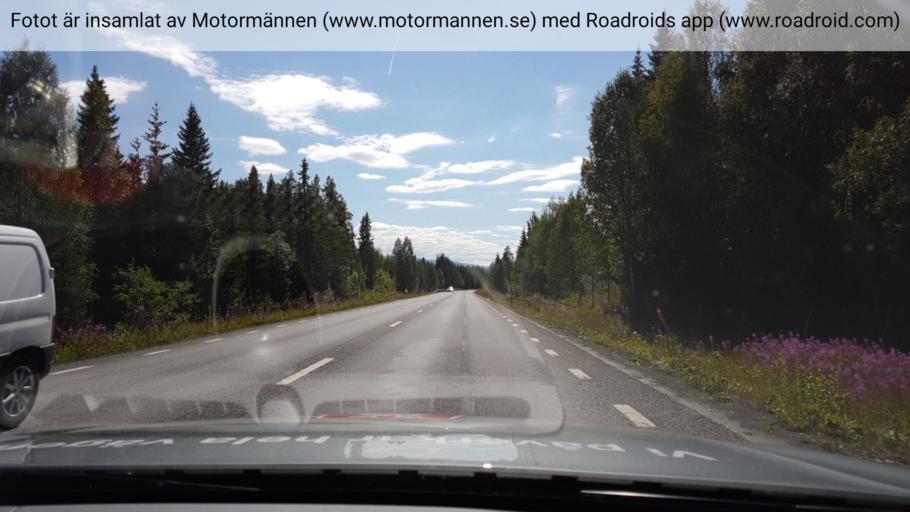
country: SE
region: Jaemtland
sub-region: Krokoms Kommun
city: Valla
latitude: 63.3149
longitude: 13.9312
